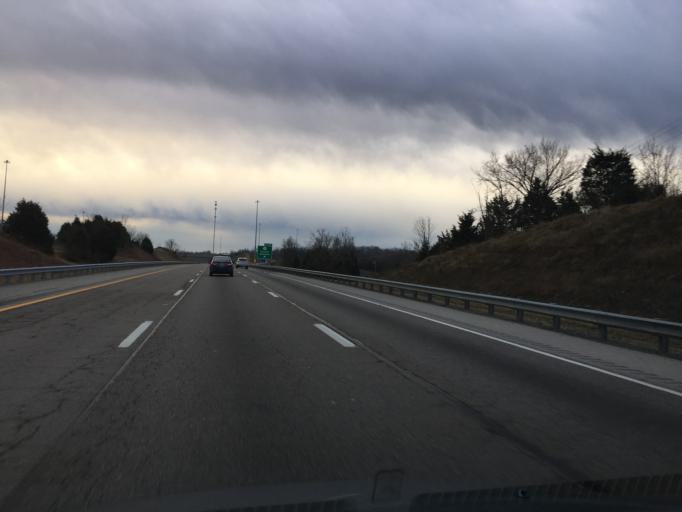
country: US
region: Kentucky
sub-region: Grant County
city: Williamstown
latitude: 38.4963
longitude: -84.5882
